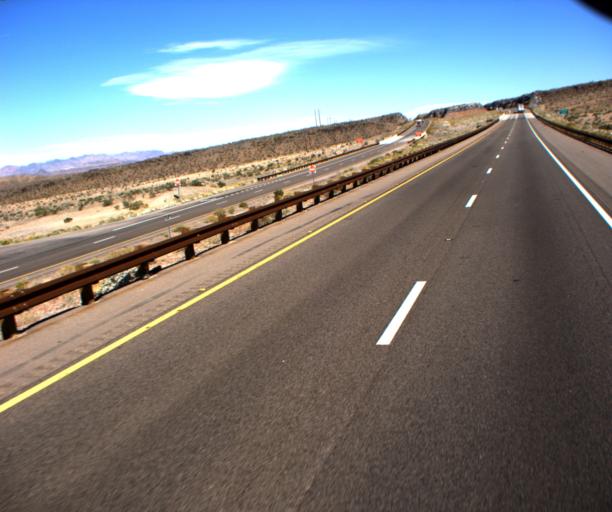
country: US
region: Nevada
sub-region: Clark County
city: Boulder City
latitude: 35.9450
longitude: -114.6441
